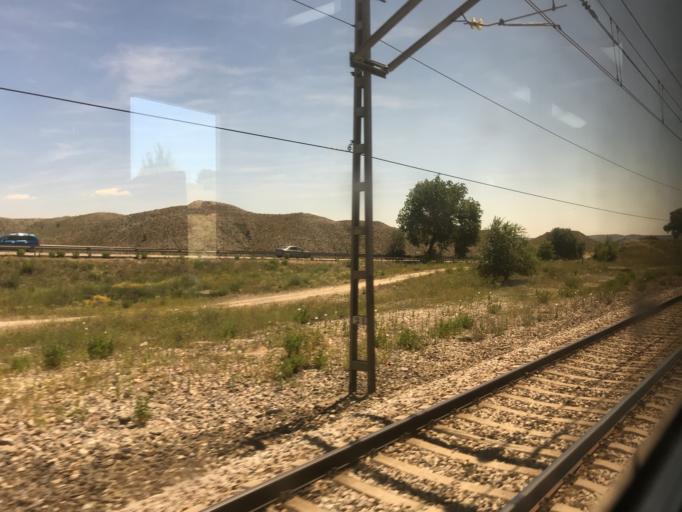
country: ES
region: Madrid
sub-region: Provincia de Madrid
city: Ciempozuelos
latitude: 40.1665
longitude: -3.6145
